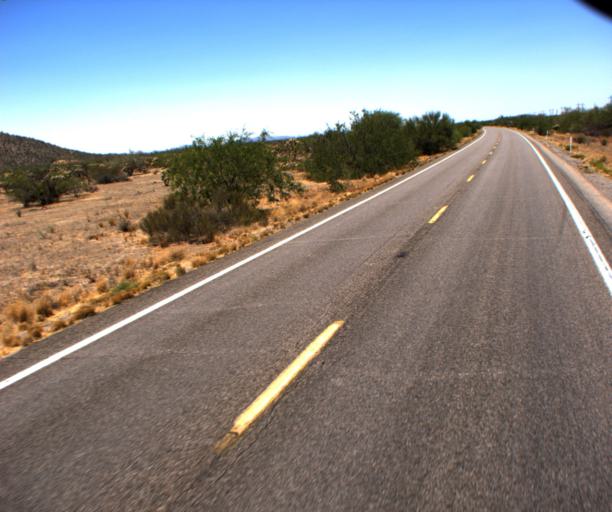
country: US
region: Arizona
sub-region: Pima County
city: Catalina
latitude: 32.7470
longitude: -111.1295
